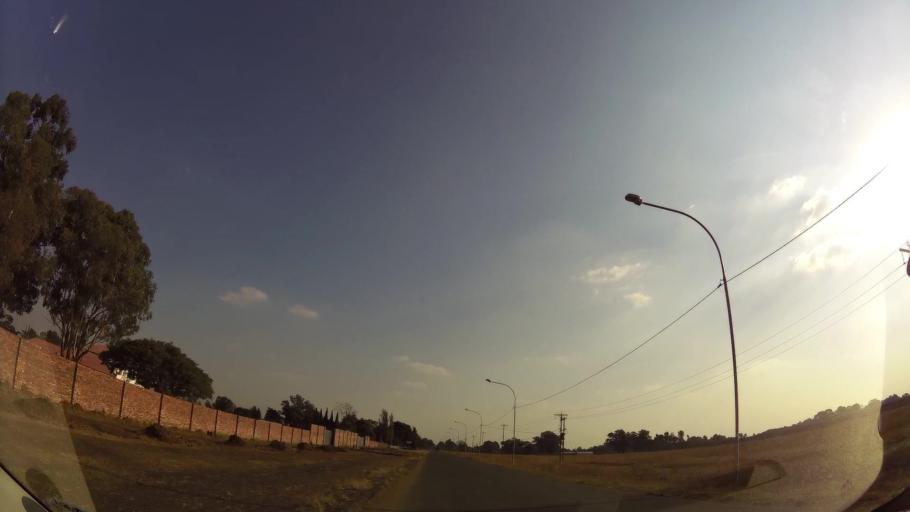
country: ZA
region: Gauteng
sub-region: Ekurhuleni Metropolitan Municipality
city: Benoni
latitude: -26.1029
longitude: 28.3826
